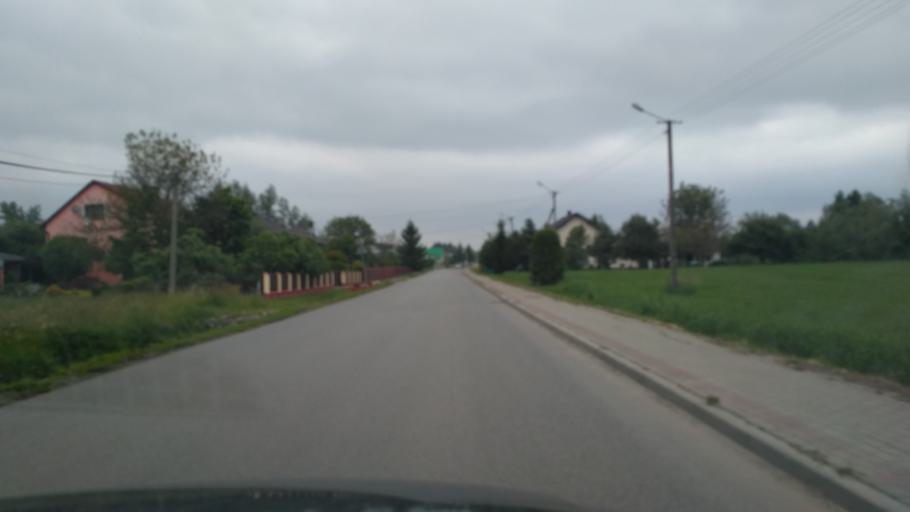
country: PL
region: Subcarpathian Voivodeship
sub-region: Powiat ropczycko-sedziszowski
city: Sedziszow Malopolski
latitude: 50.0944
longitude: 21.6640
